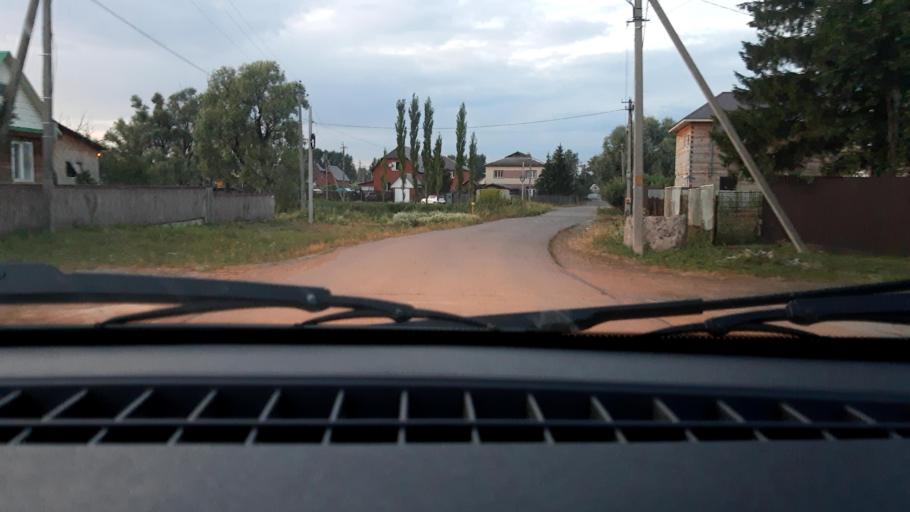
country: RU
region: Bashkortostan
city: Mikhaylovka
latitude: 54.7774
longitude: 55.8275
